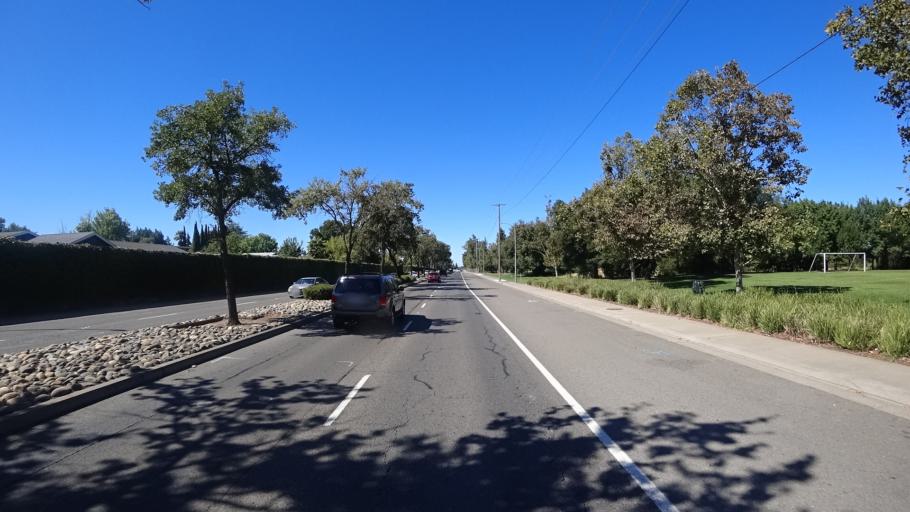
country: US
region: California
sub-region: Sacramento County
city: Elk Grove
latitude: 38.4235
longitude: -121.3788
